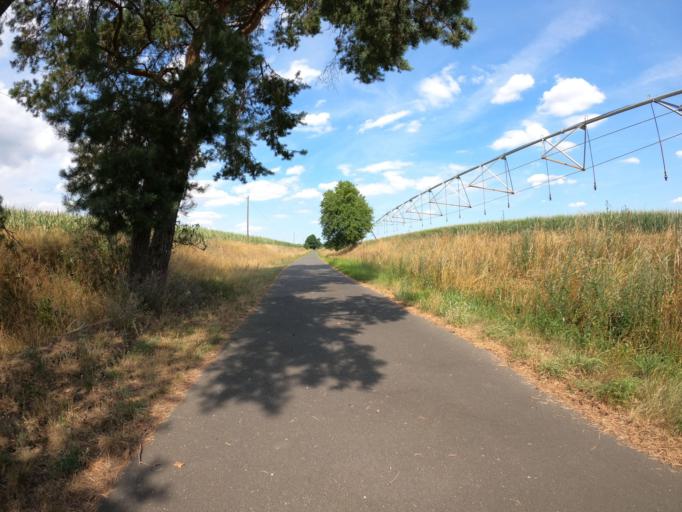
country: DE
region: Mecklenburg-Vorpommern
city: Woldegk
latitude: 53.3358
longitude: 13.5967
